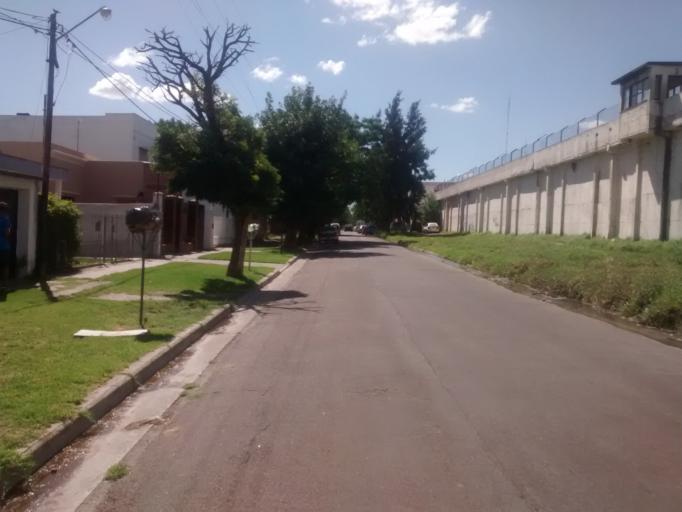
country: AR
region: Buenos Aires
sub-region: Partido de La Plata
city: La Plata
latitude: -34.9389
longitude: -57.9265
